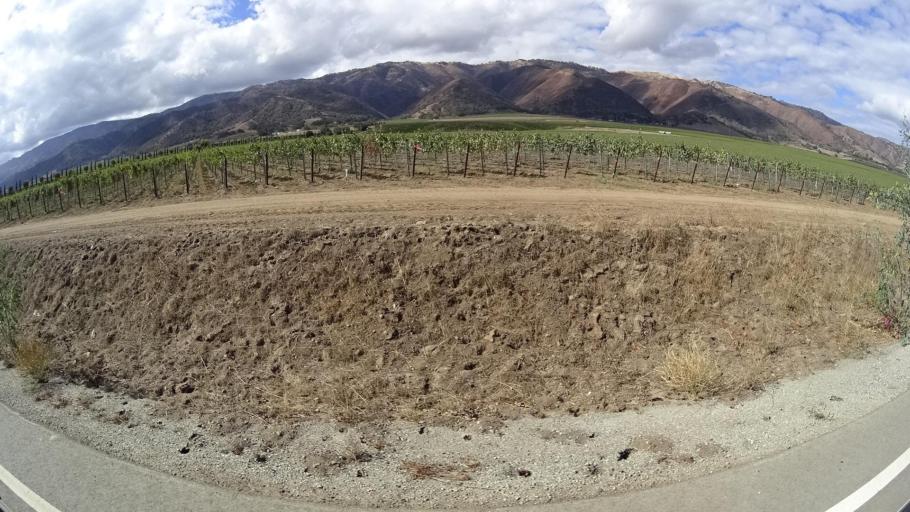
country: US
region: California
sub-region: Monterey County
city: Gonzales
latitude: 36.4900
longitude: -121.4898
